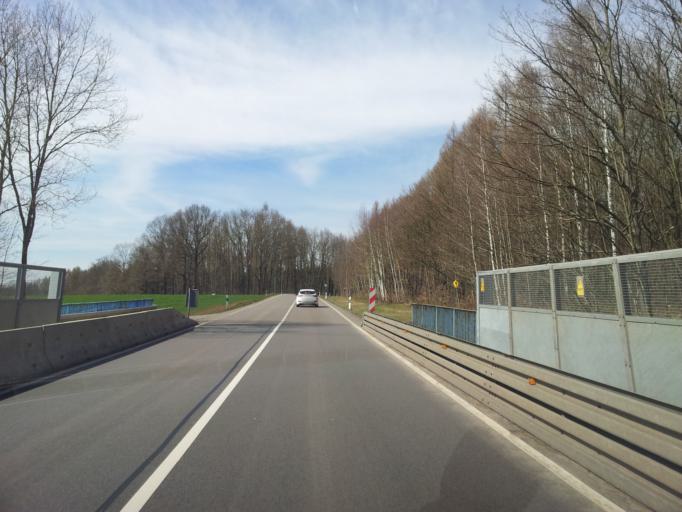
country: DE
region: Saxony
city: Bernsdorf
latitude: 50.7941
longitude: 12.6762
